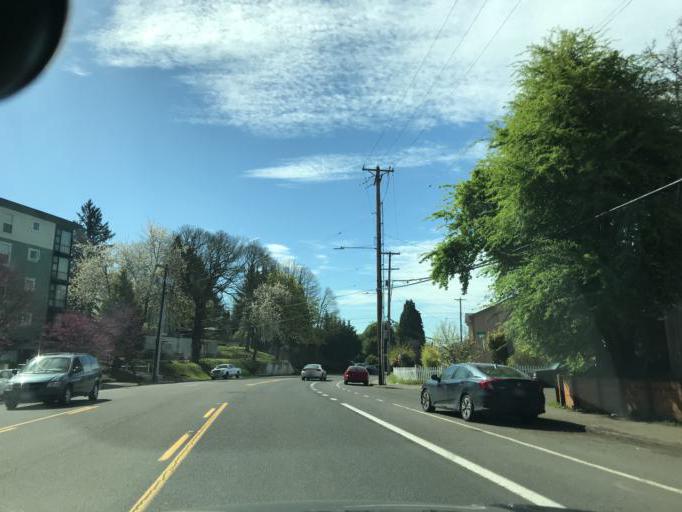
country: US
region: Oregon
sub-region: Multnomah County
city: Lents
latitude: 45.5024
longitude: -122.5684
